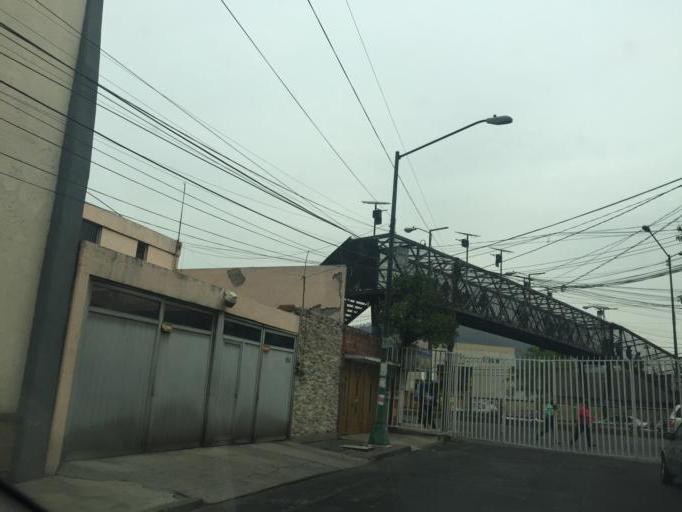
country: MX
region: Mexico
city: Colonia Lindavista
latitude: 19.4944
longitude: -99.1223
